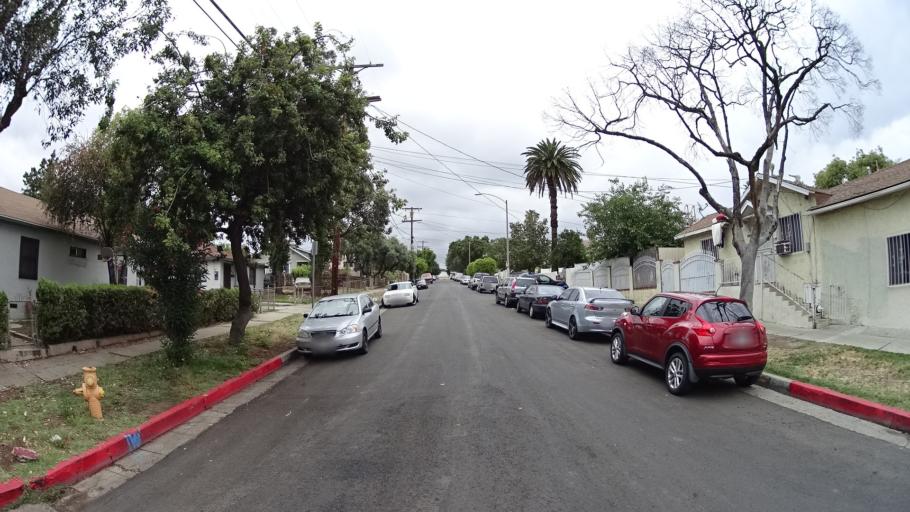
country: US
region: California
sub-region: Los Angeles County
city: Boyle Heights
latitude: 34.0604
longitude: -118.1979
